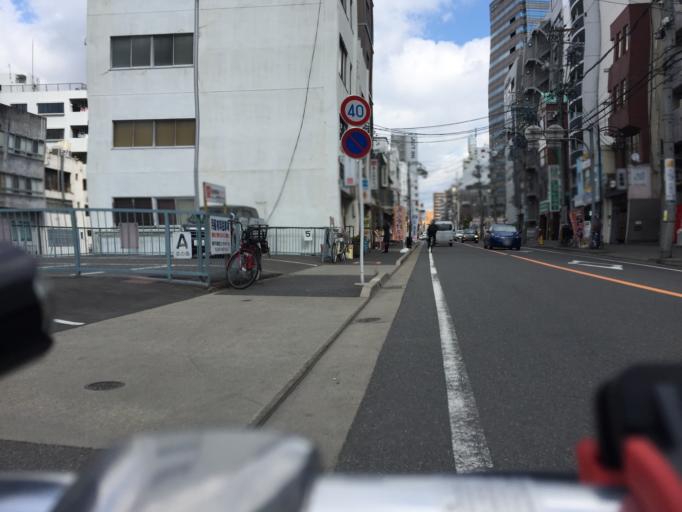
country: JP
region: Aichi
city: Nagoya-shi
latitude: 35.1708
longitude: 136.8928
